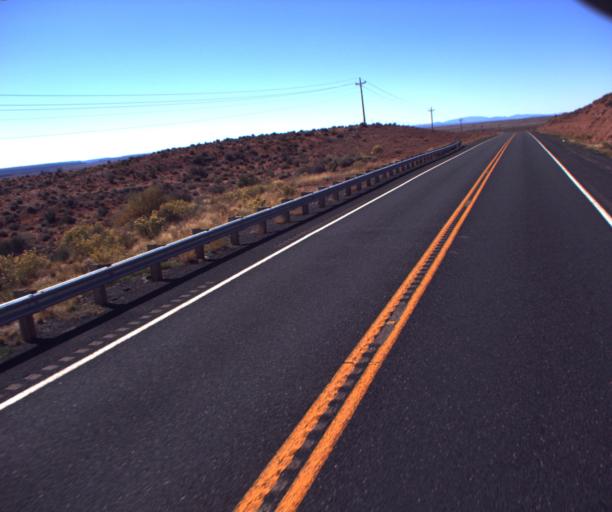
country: US
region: Arizona
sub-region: Coconino County
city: Fredonia
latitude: 36.9050
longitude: -112.5940
